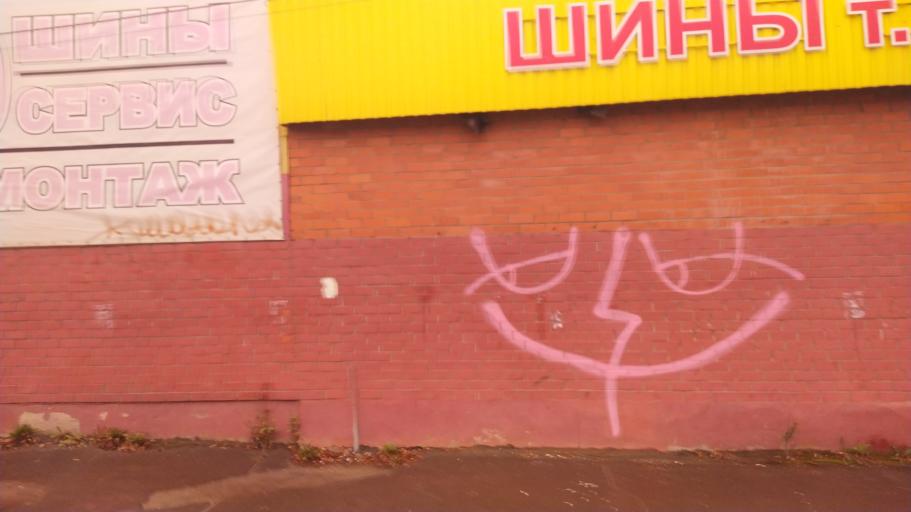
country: RU
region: Tverskaya
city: Tver
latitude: 56.8351
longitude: 35.9058
